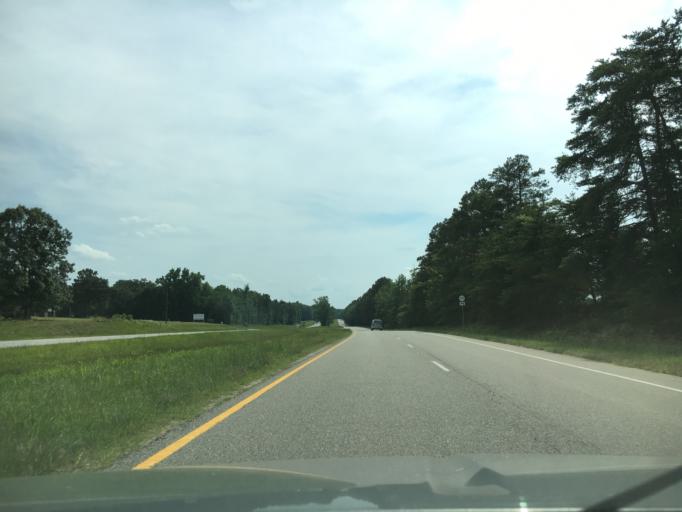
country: US
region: Virginia
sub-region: Nottoway County
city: Crewe
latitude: 37.2134
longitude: -78.1543
